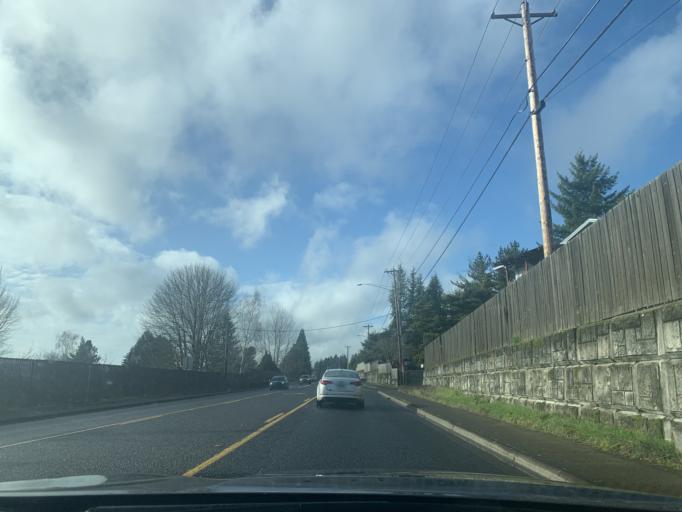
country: US
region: Oregon
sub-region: Washington County
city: King City
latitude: 45.4102
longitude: -122.7992
